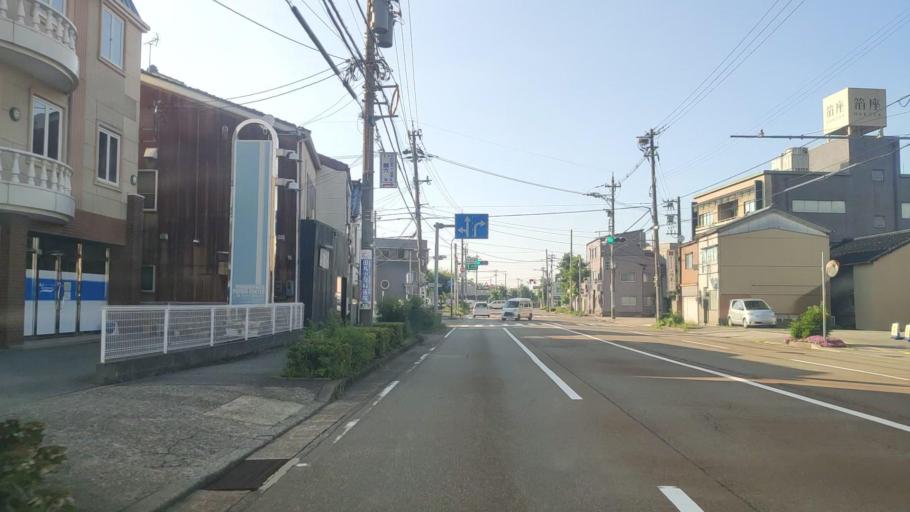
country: JP
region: Ishikawa
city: Kanazawa-shi
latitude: 36.5770
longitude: 136.6650
